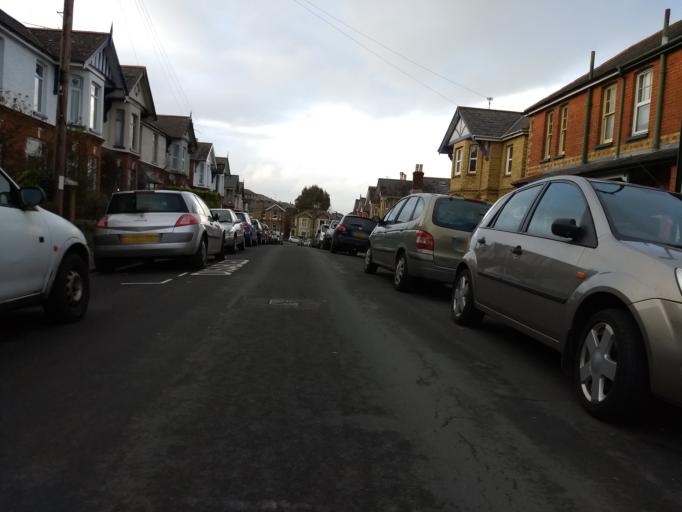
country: GB
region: England
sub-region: Isle of Wight
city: Ryde
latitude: 50.7233
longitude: -1.1646
